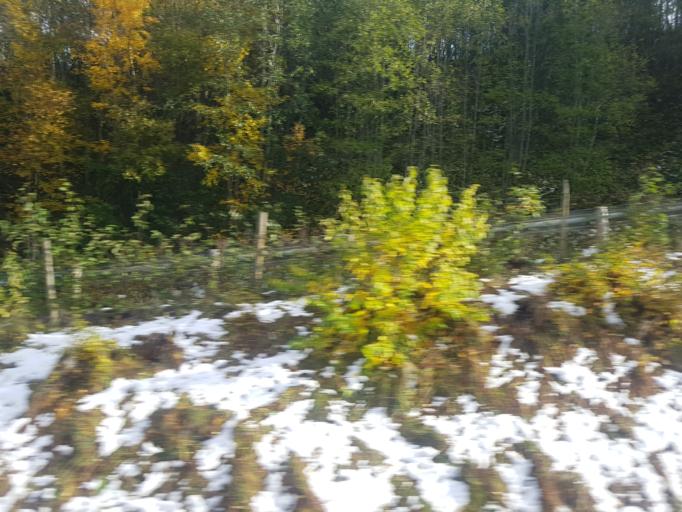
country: NO
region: Oppland
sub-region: Dovre
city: Dombas
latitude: 62.0454
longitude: 9.1460
